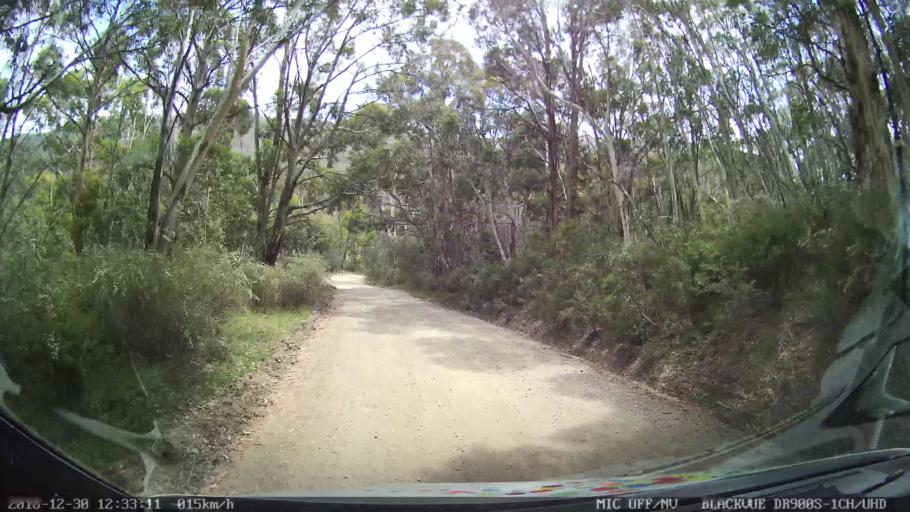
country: AU
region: New South Wales
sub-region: Snowy River
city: Jindabyne
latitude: -36.3239
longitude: 148.4677
